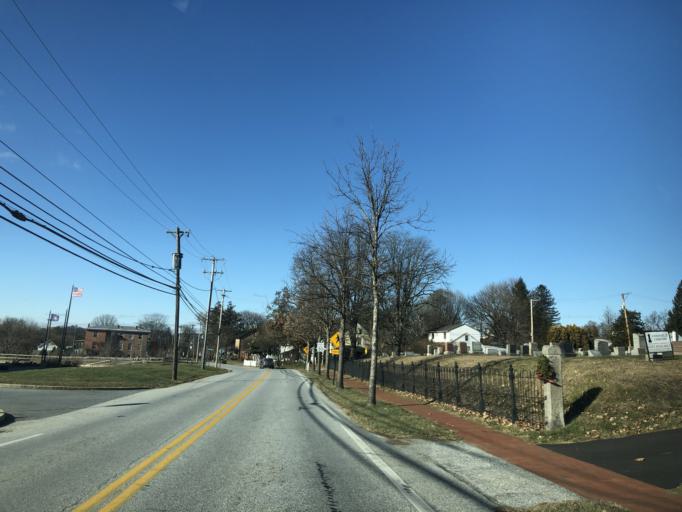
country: US
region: Pennsylvania
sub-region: Chester County
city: Upland
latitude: 39.8944
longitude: -75.7296
